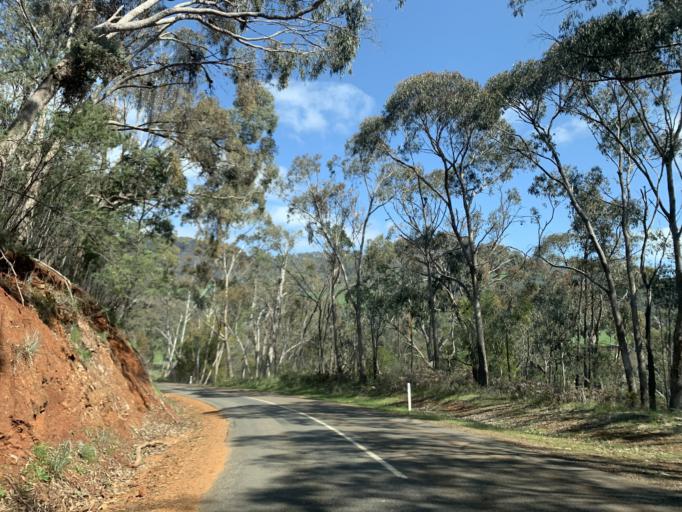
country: AU
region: Victoria
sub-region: Mansfield
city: Mansfield
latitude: -36.8266
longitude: 146.1300
